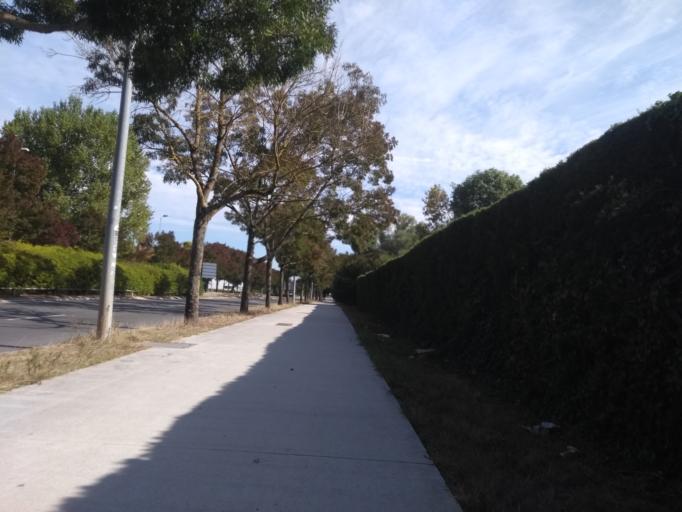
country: FR
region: Aquitaine
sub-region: Departement de la Gironde
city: Le Bouscat
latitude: 44.8913
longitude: -0.5645
